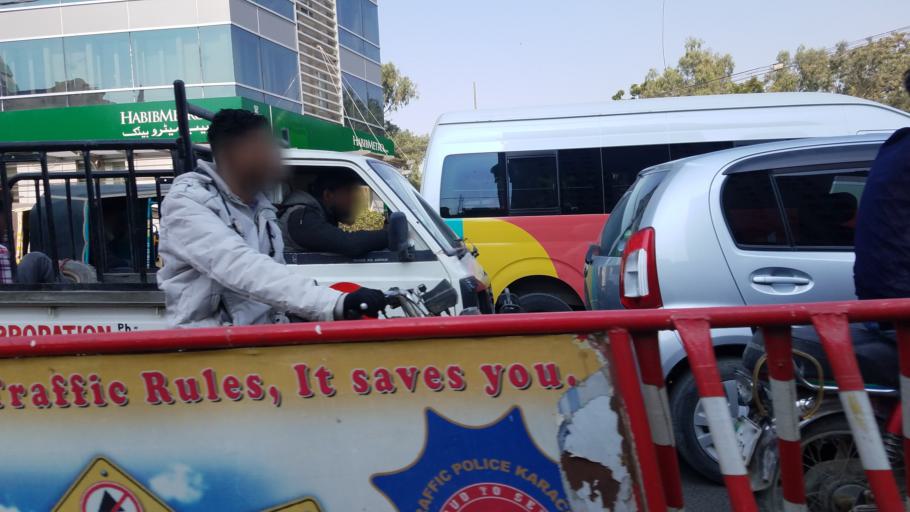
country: PK
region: Sindh
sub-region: Karachi District
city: Karachi
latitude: 24.8508
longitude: 67.0182
